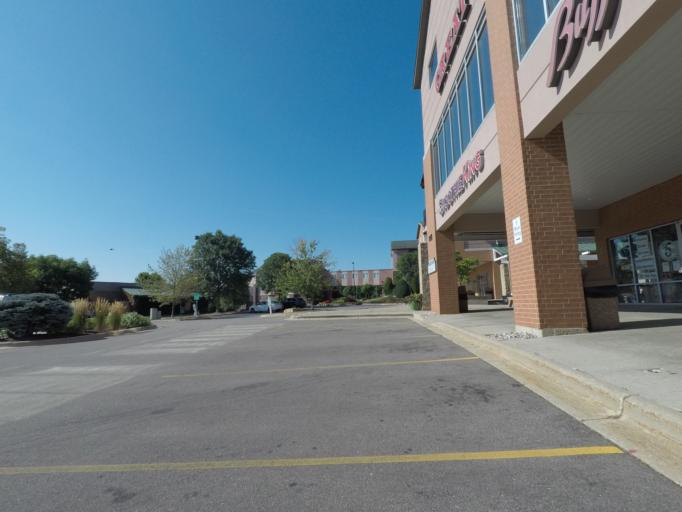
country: US
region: Wisconsin
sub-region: Dane County
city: Madison
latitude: 43.0177
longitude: -89.4232
